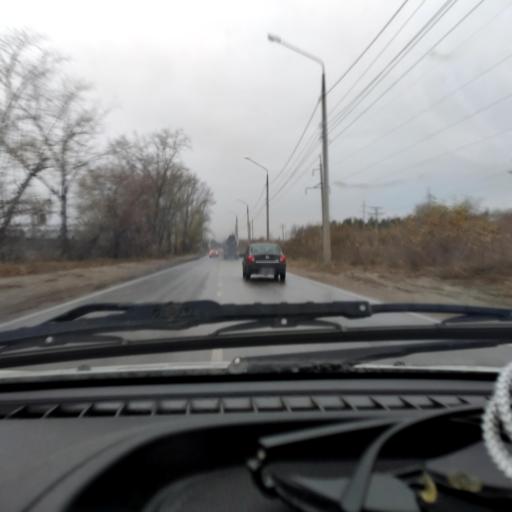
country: RU
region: Samara
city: Zhigulevsk
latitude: 53.4638
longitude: 49.5540
